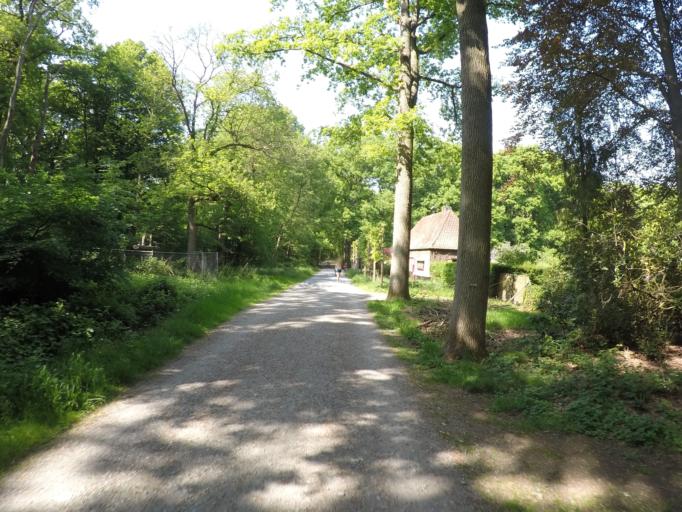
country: BE
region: Flanders
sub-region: Provincie Antwerpen
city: Brasschaat
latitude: 51.2739
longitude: 4.4845
